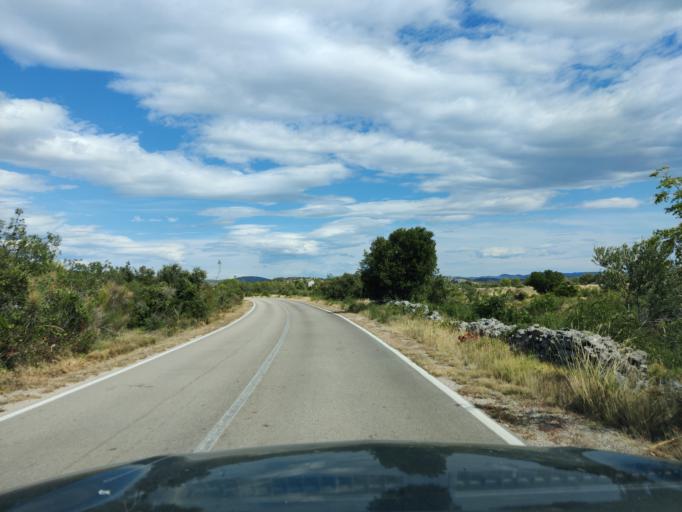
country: HR
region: Sibensko-Kniniska
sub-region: Grad Sibenik
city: Sibenik
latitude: 43.7420
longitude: 15.8540
